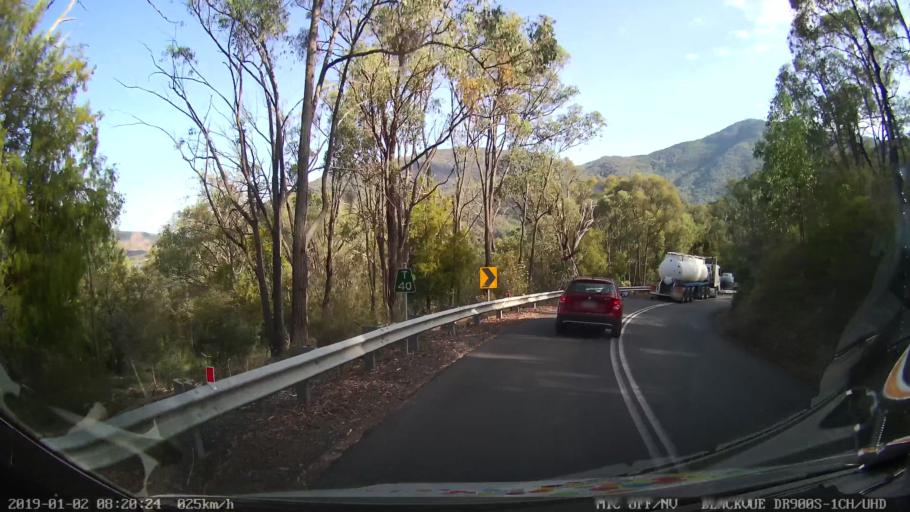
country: AU
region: New South Wales
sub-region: Tumut Shire
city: Tumut
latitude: -35.5725
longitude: 148.3239
